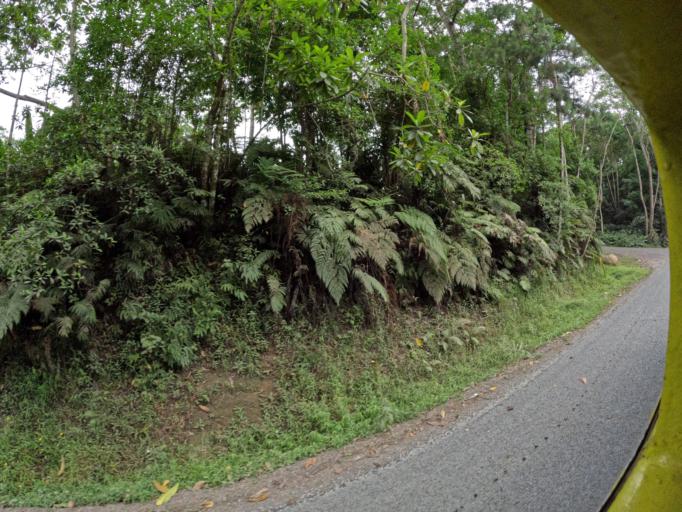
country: FJ
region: Central
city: Suva
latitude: -18.0615
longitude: 178.4570
